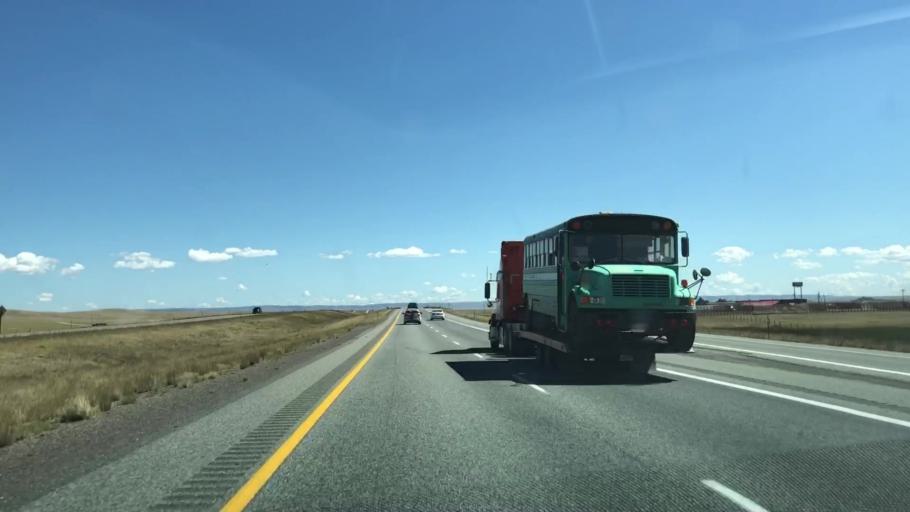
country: US
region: Wyoming
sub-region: Albany County
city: Laramie
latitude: 41.4414
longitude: -105.9481
